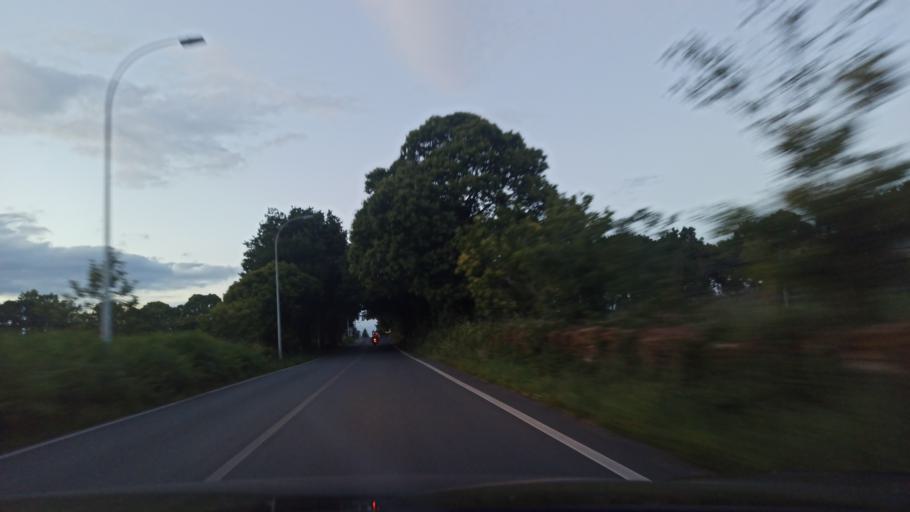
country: ES
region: Galicia
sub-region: Provincia de Lugo
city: Lugo
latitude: 42.9837
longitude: -7.5835
